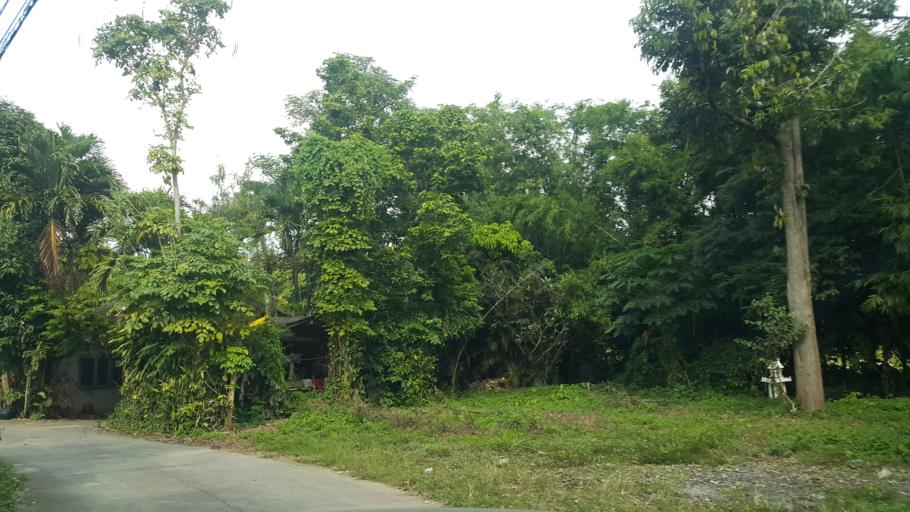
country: TH
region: Chiang Mai
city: San Sai
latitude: 18.9068
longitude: 99.1290
